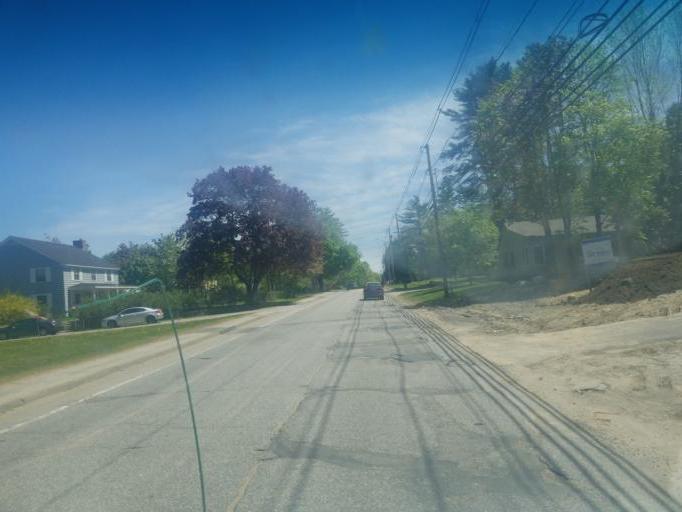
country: US
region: New Hampshire
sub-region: Grafton County
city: Plymouth
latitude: 43.7618
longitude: -71.7051
